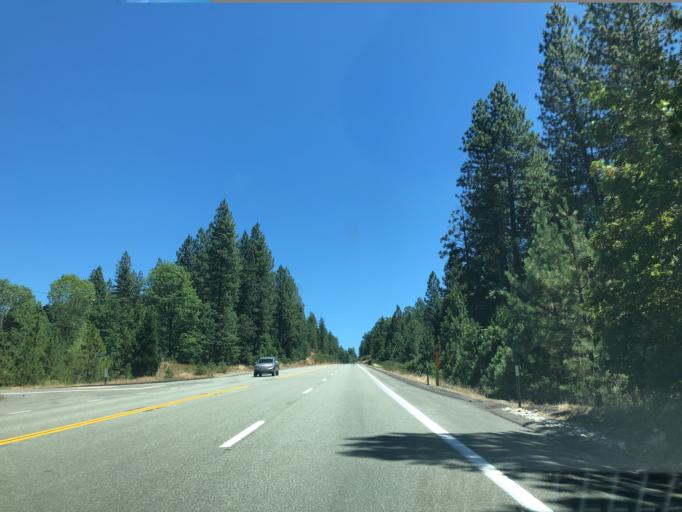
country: US
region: California
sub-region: Shasta County
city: Shingletown
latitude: 40.5000
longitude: -121.9260
